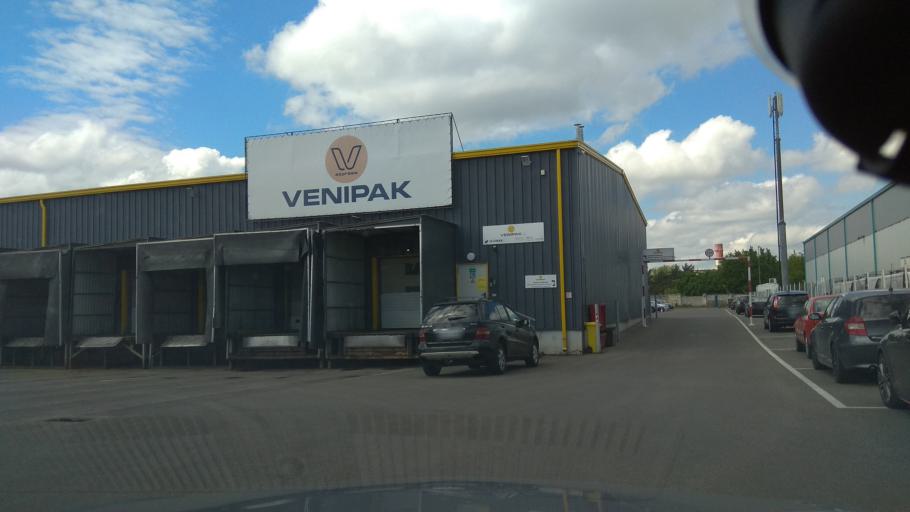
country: LT
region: Vilnius County
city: Vilkpede
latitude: 54.6640
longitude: 25.2464
